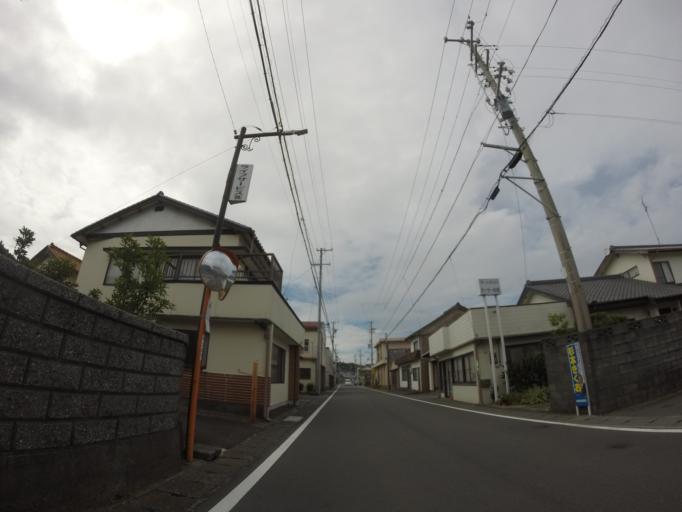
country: JP
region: Shizuoka
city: Oyama
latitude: 34.6320
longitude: 138.1949
